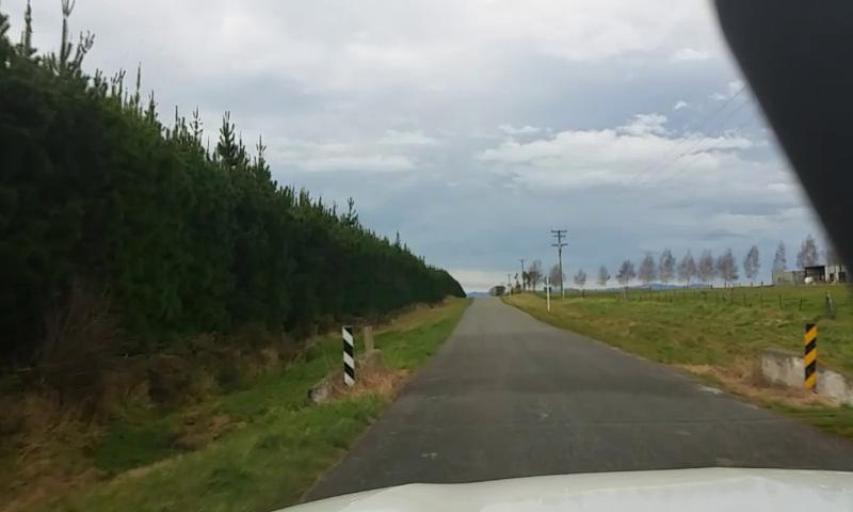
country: NZ
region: Canterbury
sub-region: Waimakariri District
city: Kaiapoi
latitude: -43.2915
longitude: 172.4706
